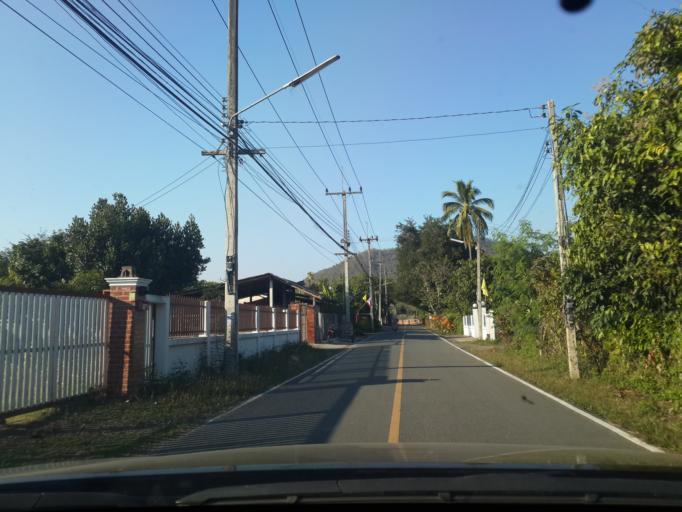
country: TH
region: Chiang Mai
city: San Sai
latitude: 18.9162
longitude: 99.1327
